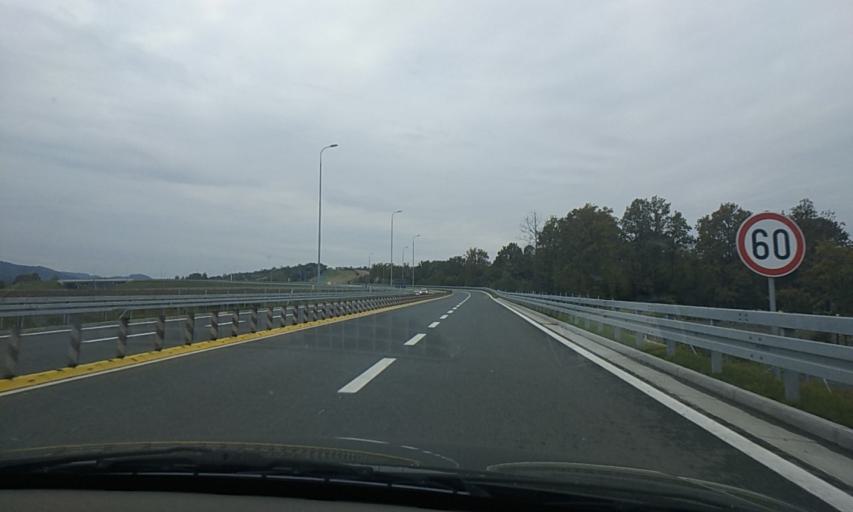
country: BA
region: Republika Srpska
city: Prnjavor
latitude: 44.8518
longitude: 17.6817
